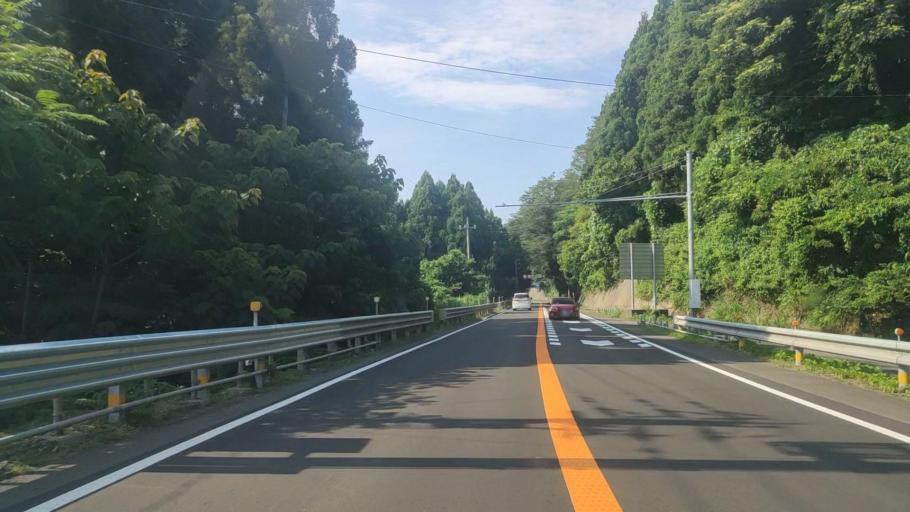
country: JP
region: Fukui
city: Takefu
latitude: 35.7927
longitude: 136.0927
